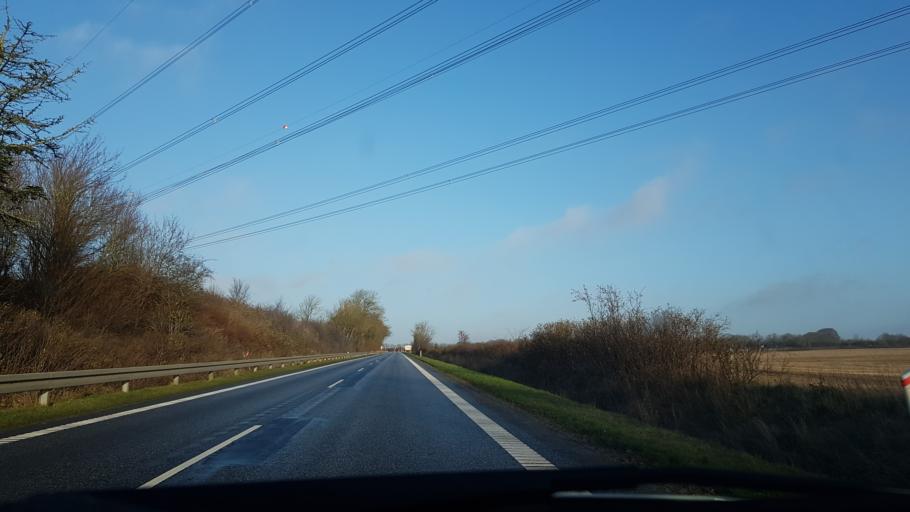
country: DK
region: South Denmark
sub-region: Tonder Kommune
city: Toftlund
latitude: 55.2496
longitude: 9.1409
